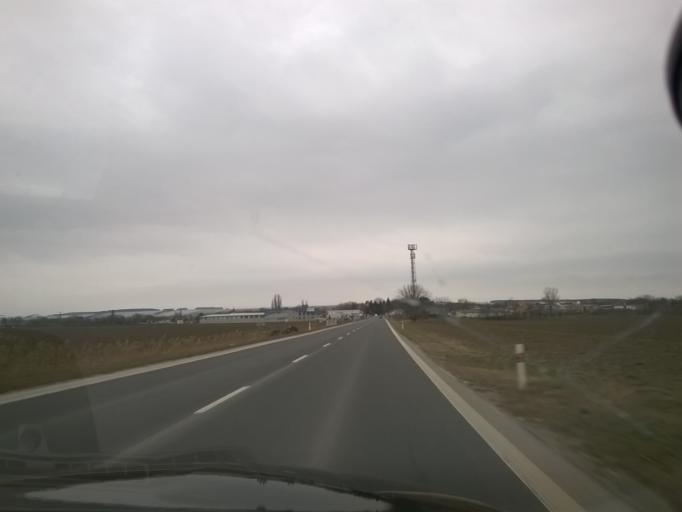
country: SK
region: Nitriansky
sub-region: Okres Nitra
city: Nitra
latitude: 48.3753
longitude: 18.0478
